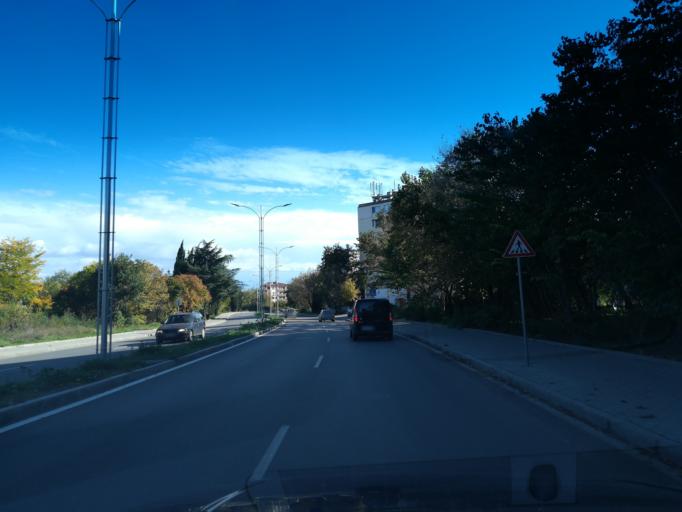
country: BG
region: Stara Zagora
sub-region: Obshtina Stara Zagora
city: Stara Zagora
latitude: 42.4299
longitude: 25.6449
